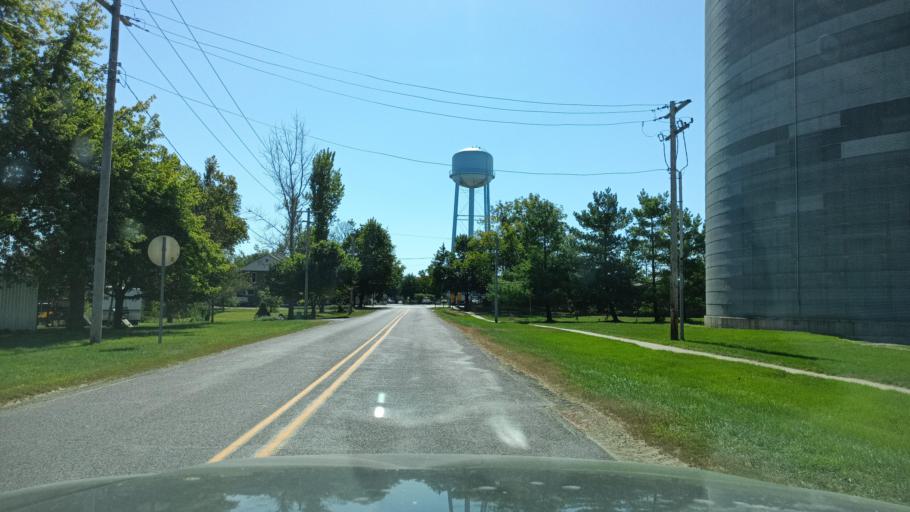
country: US
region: Illinois
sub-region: McLean County
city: Danvers
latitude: 40.6149
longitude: -89.2045
